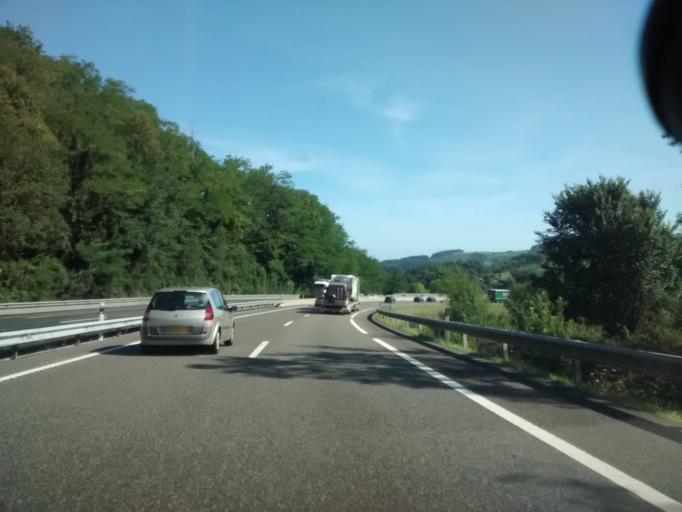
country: ES
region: Basque Country
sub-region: Provincia de Guipuzcoa
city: Zumaia
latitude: 43.2754
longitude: -2.2552
